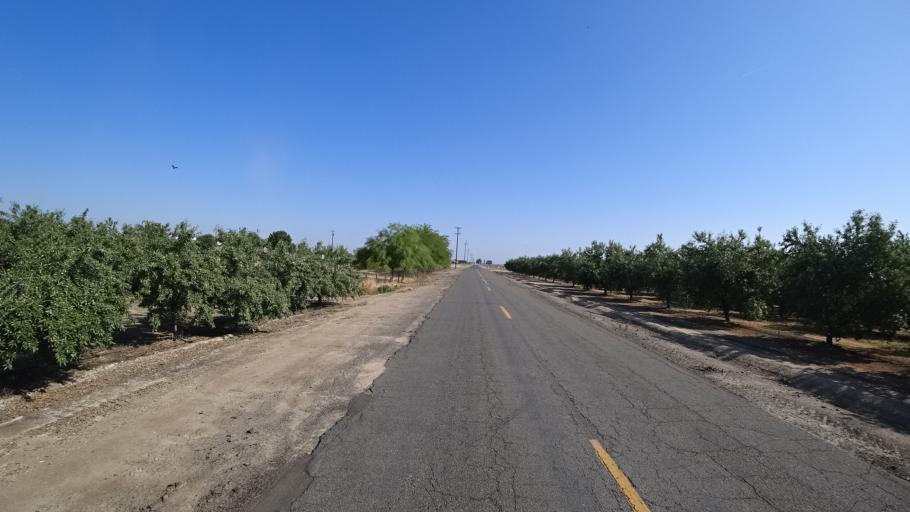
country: US
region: California
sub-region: Kings County
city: Home Garden
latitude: 36.2248
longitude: -119.5831
